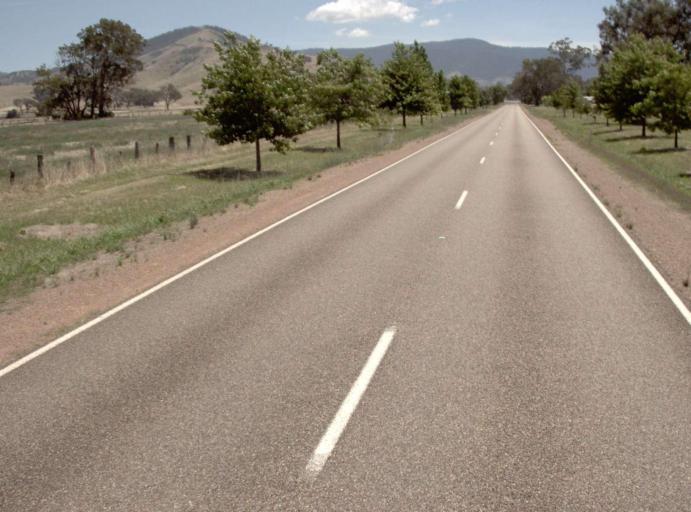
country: AU
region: Victoria
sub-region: East Gippsland
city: Bairnsdale
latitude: -37.2485
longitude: 147.7124
